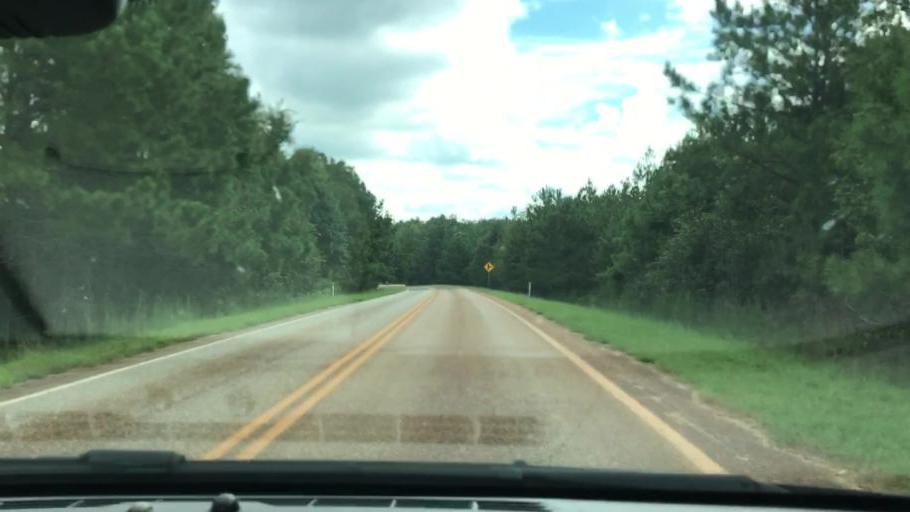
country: US
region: Georgia
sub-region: Stewart County
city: Lumpkin
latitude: 32.0715
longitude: -84.8707
